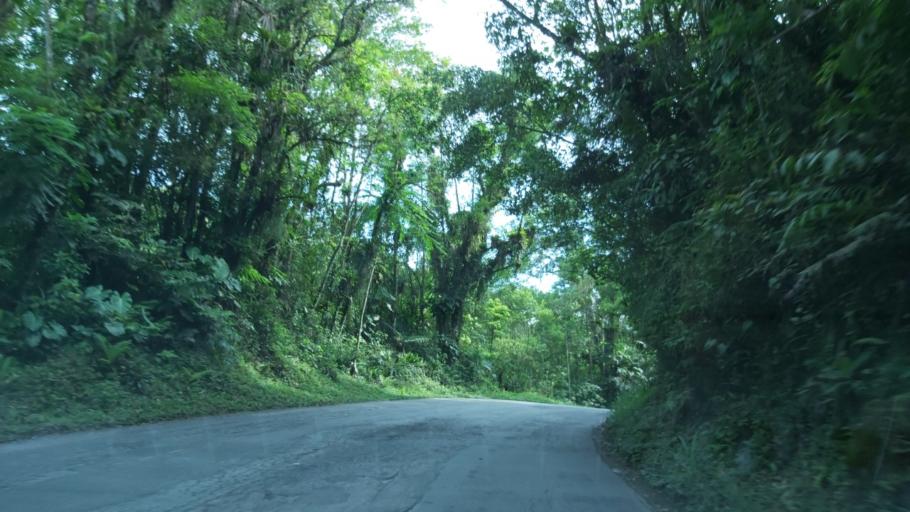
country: BR
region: Sao Paulo
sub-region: Miracatu
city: Miracatu
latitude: -24.0572
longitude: -47.5868
